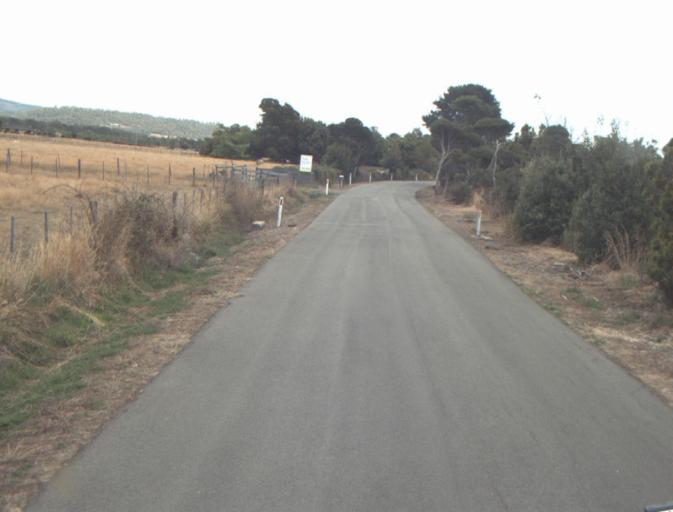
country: AU
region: Tasmania
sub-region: Launceston
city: Mayfield
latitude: -41.2842
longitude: 147.0047
